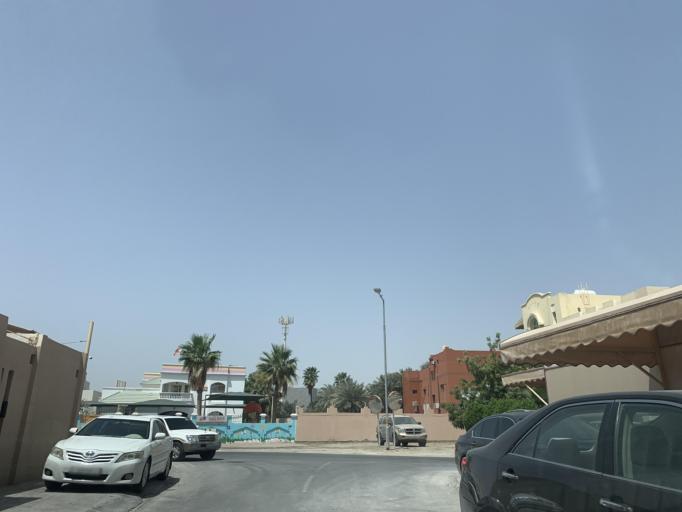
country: BH
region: Northern
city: Sitrah
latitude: 26.1570
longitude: 50.5837
